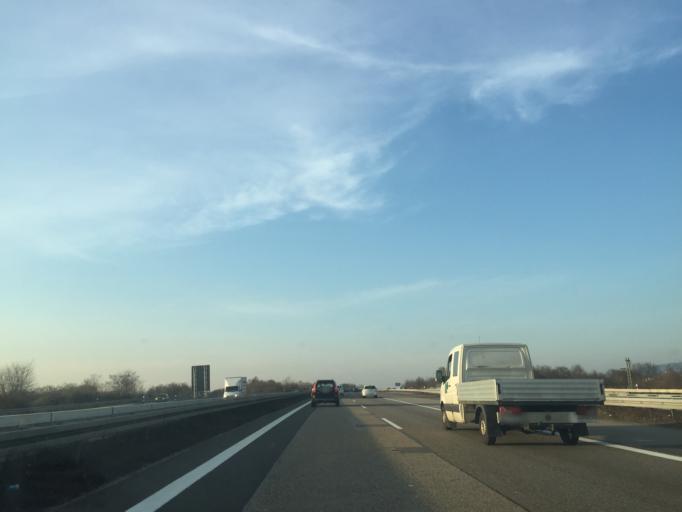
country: DE
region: Baden-Wuerttemberg
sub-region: Karlsruhe Region
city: Eppelheim
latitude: 49.4134
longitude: 8.6344
